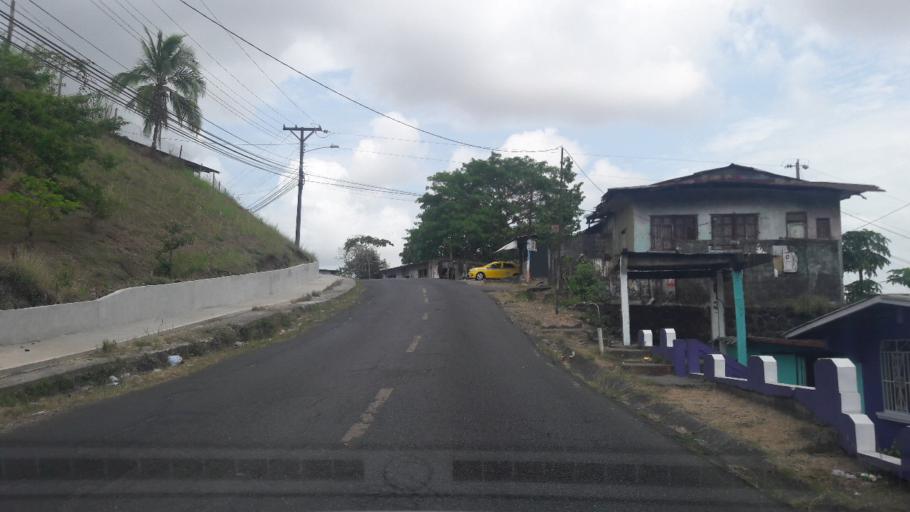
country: PA
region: Panama
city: Alcalde Diaz
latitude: 9.1143
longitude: -79.5555
